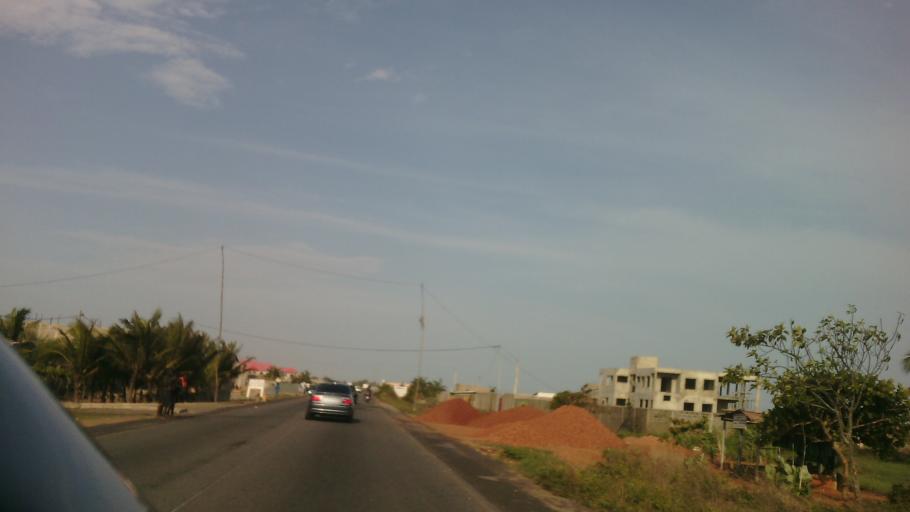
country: TG
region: Maritime
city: Lome
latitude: 6.1792
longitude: 1.3818
